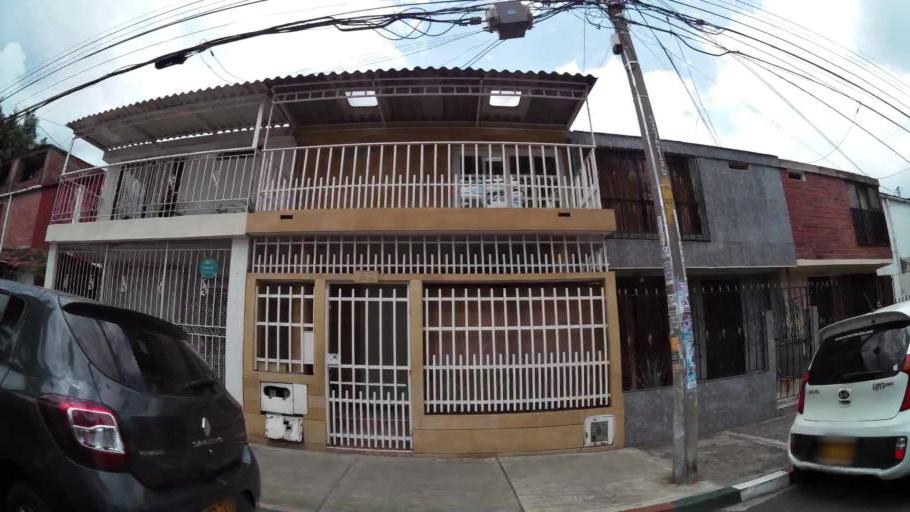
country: CO
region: Valle del Cauca
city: Cali
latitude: 3.4659
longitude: -76.4953
